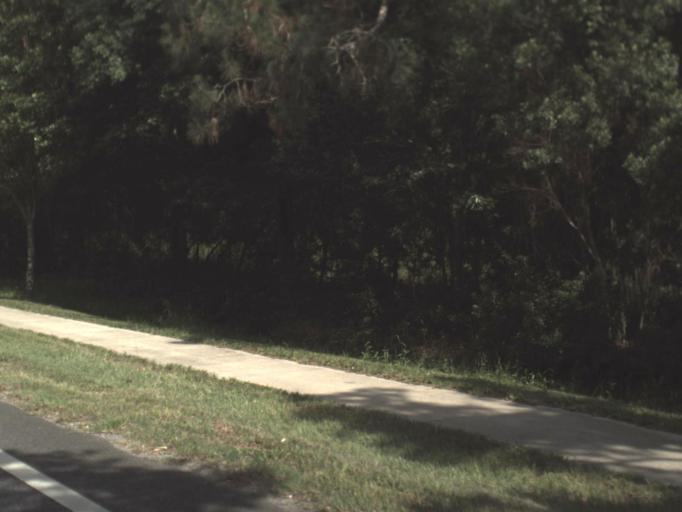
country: US
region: Florida
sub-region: Clay County
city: Asbury Lake
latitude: 29.9823
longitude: -81.8239
